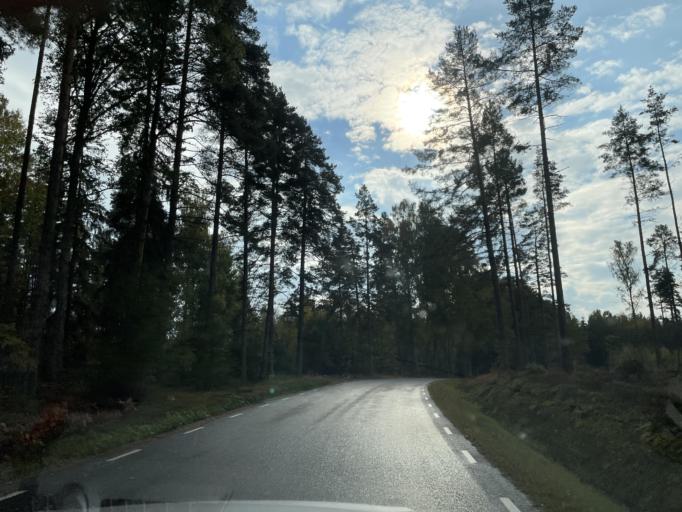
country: SE
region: Vaermland
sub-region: Karlstads Kommun
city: Skattkarr
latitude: 59.4089
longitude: 13.6025
